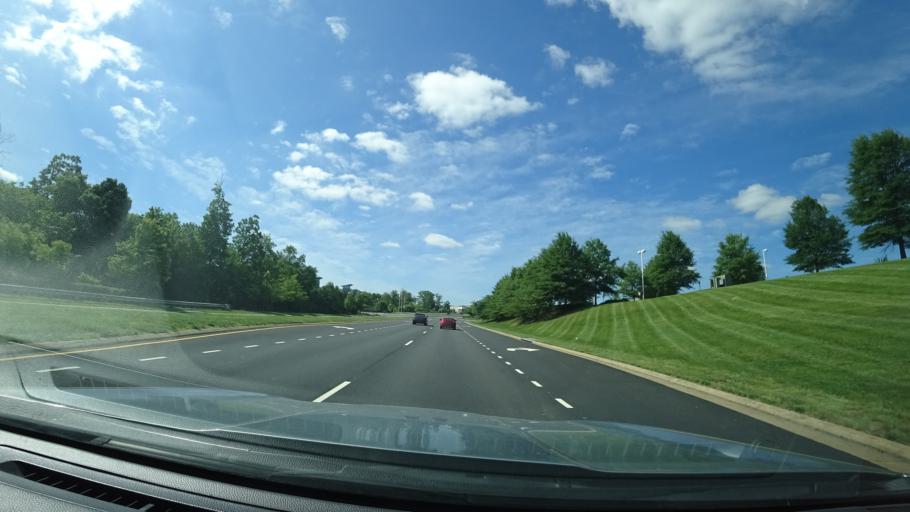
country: US
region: Virginia
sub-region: Loudoun County
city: Dulles Town Center
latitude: 39.0310
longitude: -77.4190
